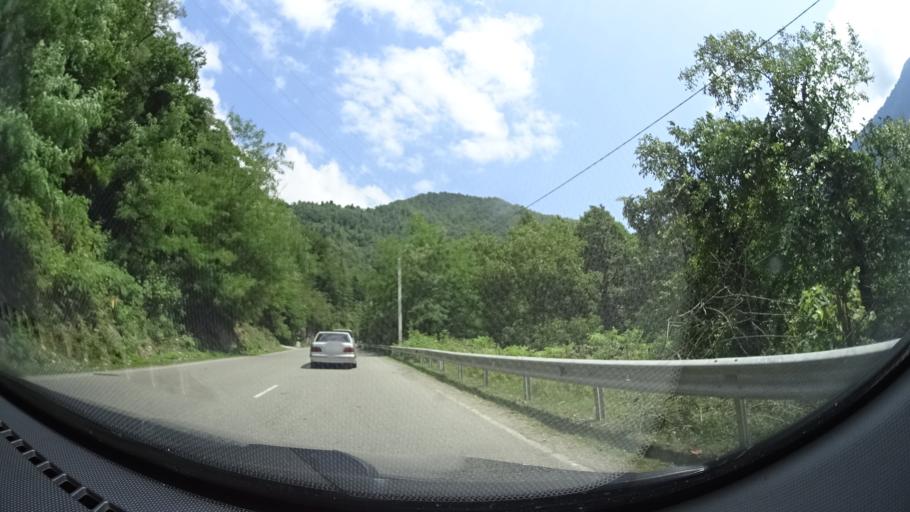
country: GE
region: Ajaria
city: Keda
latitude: 41.5712
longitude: 41.8555
